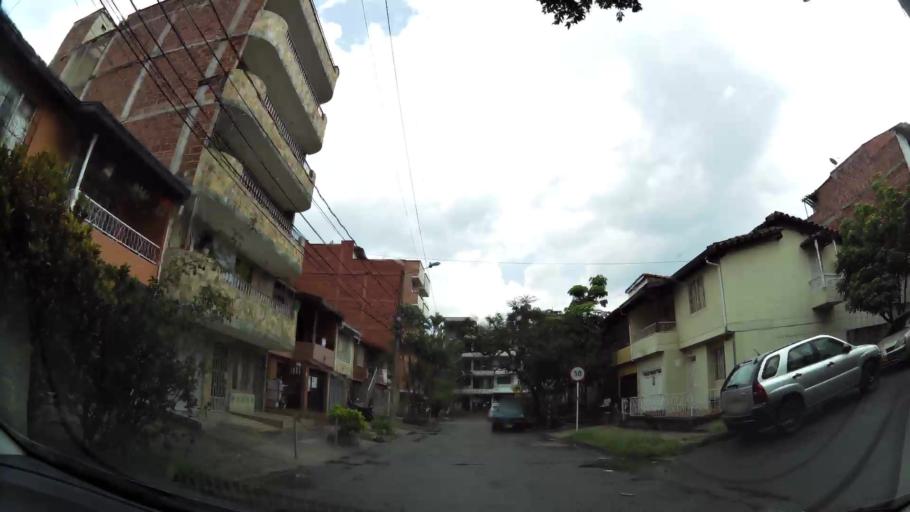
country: CO
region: Antioquia
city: Itagui
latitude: 6.1848
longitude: -75.5978
